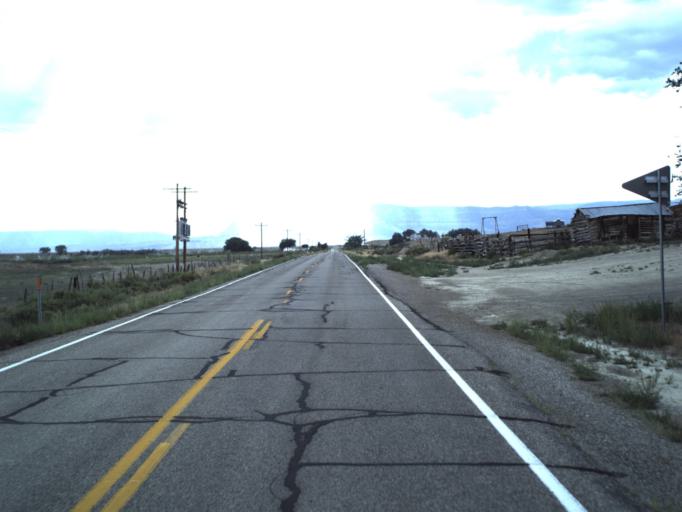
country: US
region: Utah
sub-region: Emery County
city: Huntington
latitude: 39.3474
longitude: -110.8720
